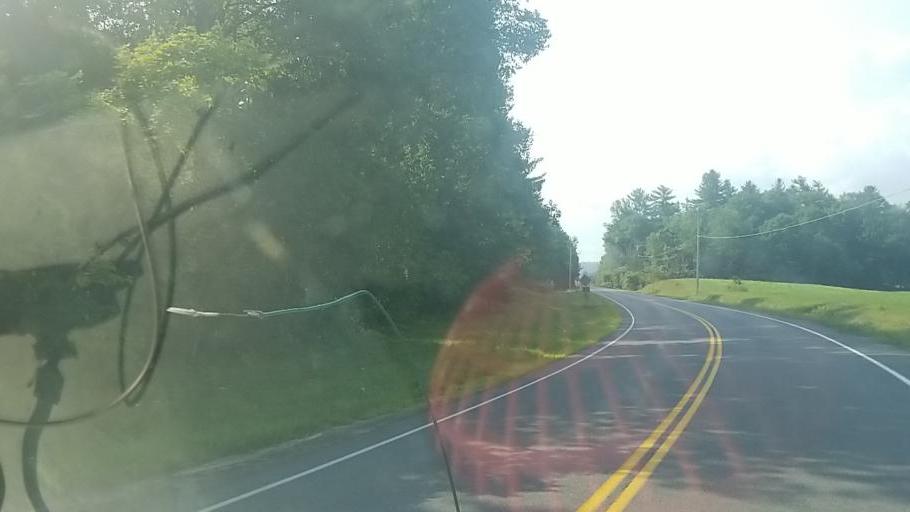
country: US
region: New York
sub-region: Fulton County
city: Gloversville
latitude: 43.0966
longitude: -74.3195
